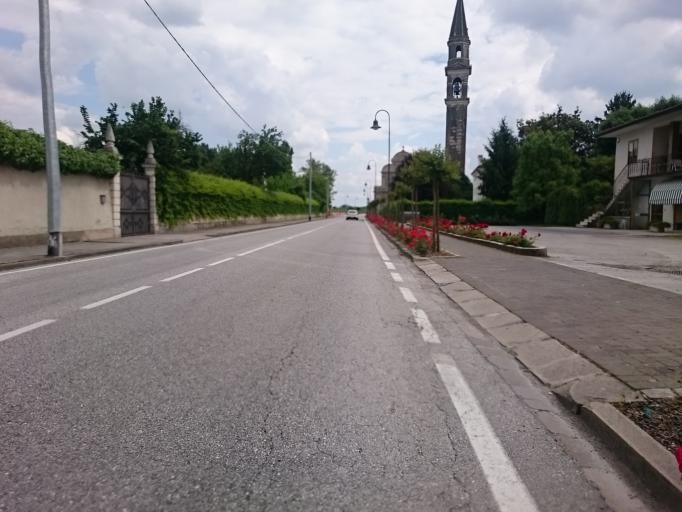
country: IT
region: Veneto
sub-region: Provincia di Vicenza
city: Montegaldella
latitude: 45.4366
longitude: 11.6736
